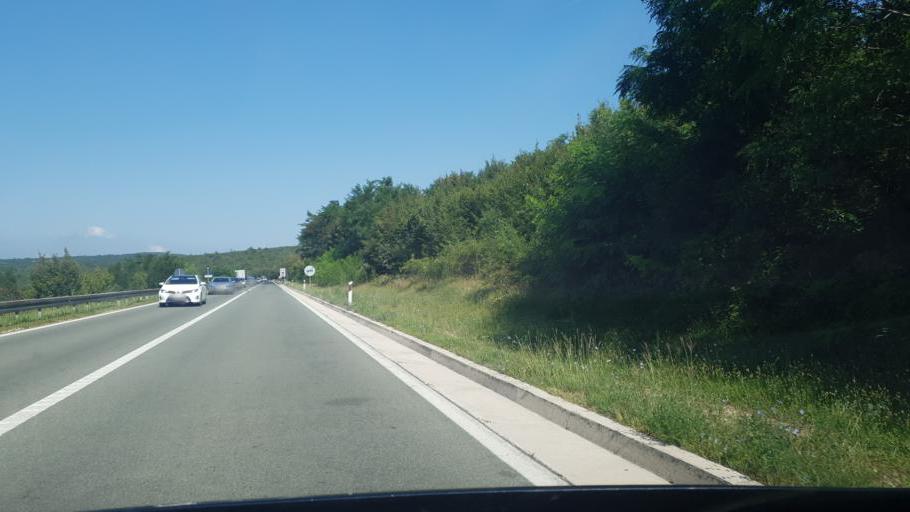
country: HR
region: Istarska
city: Buzet
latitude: 45.3475
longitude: 14.1051
